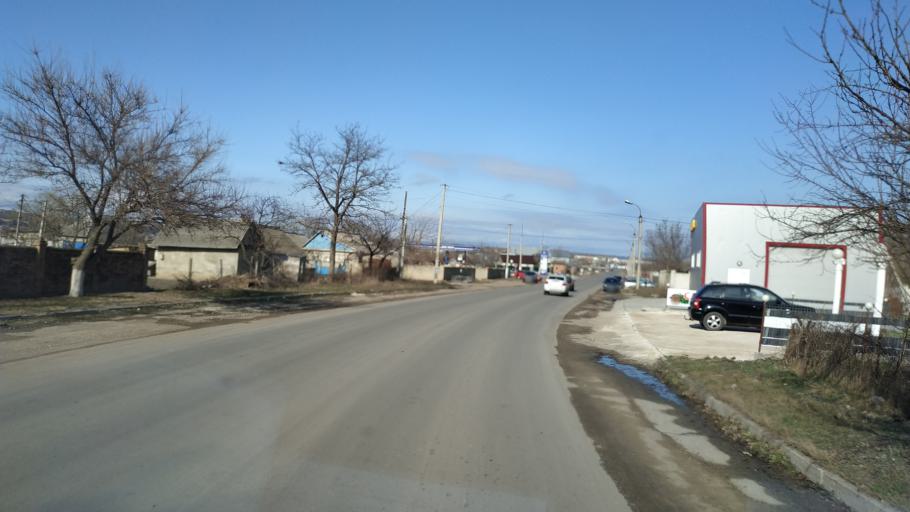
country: MD
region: Causeni
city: Causeni
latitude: 46.6409
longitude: 29.4035
